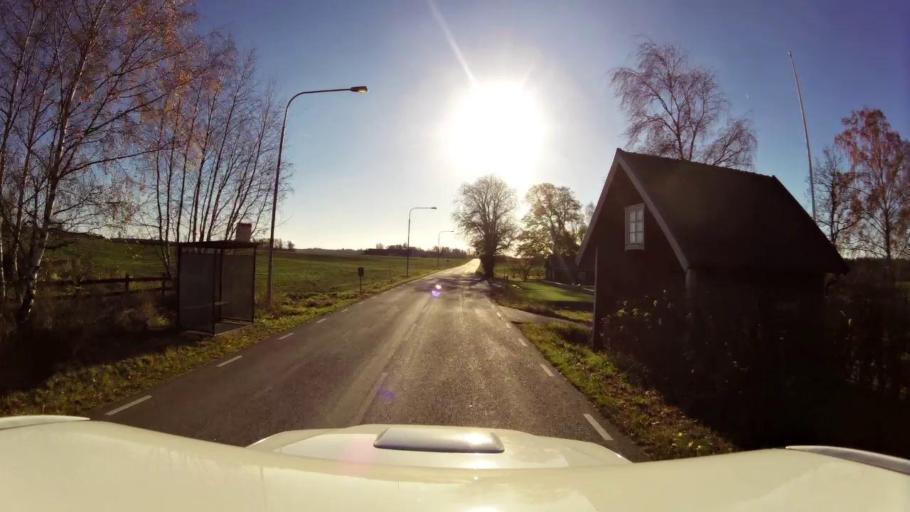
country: SE
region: OEstergoetland
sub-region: Linkopings Kommun
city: Malmslatt
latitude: 58.3574
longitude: 15.5636
